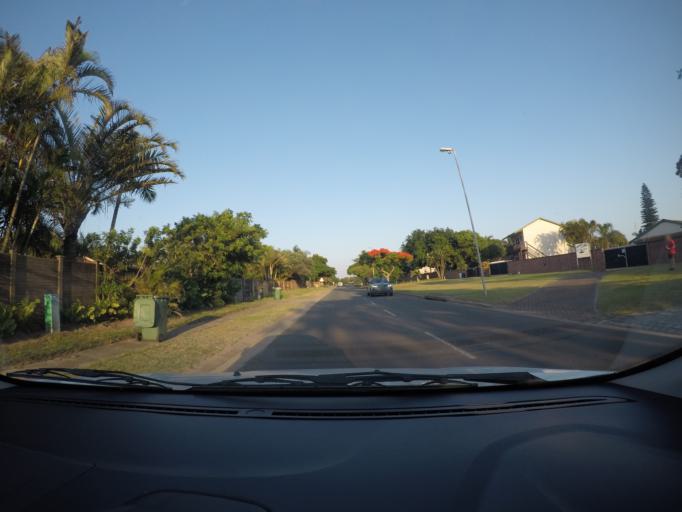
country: ZA
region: KwaZulu-Natal
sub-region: uThungulu District Municipality
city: Richards Bay
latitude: -28.7767
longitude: 32.1035
